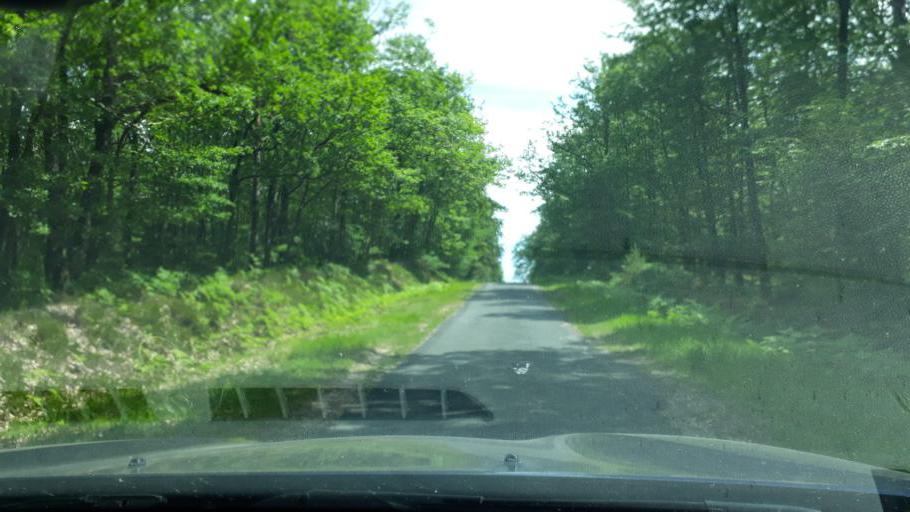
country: FR
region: Centre
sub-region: Departement du Loiret
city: Vitry-aux-Loges
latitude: 48.0236
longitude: 2.2760
